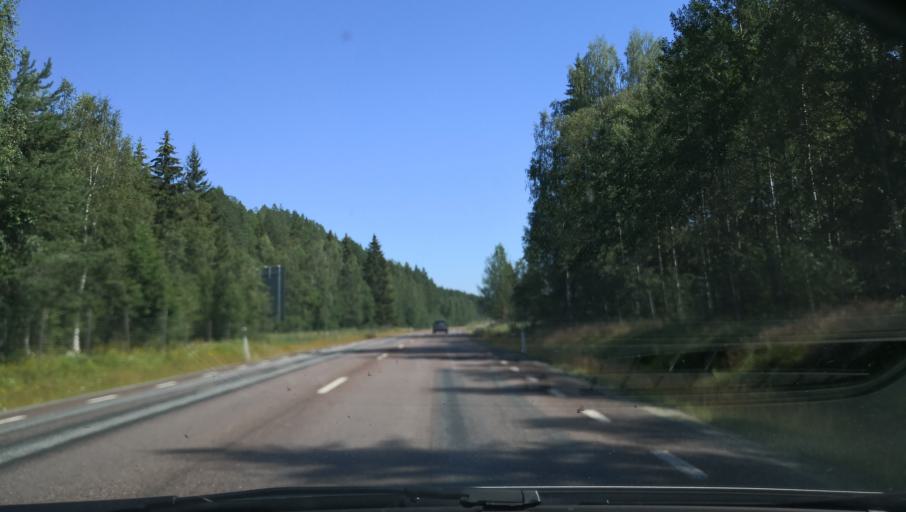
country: SE
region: Gaevleborg
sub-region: Ovanakers Kommun
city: Alfta
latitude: 61.3439
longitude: 16.1113
